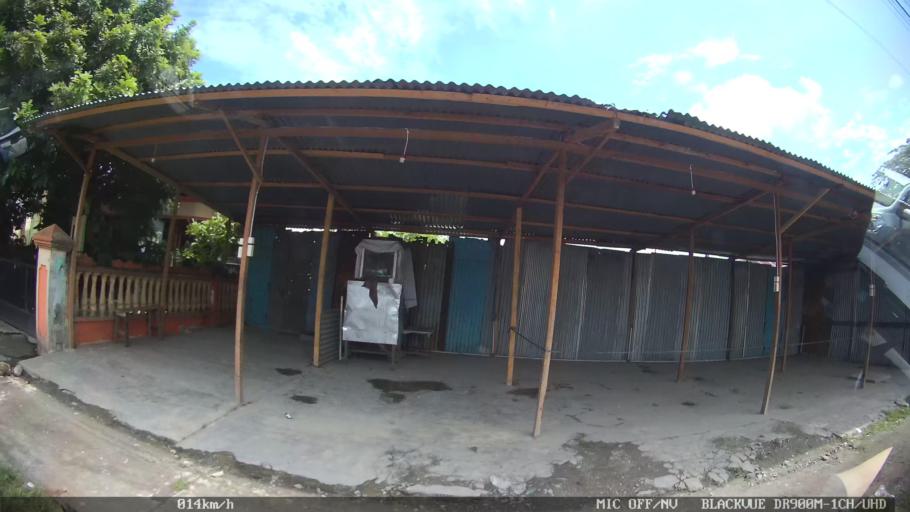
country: ID
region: North Sumatra
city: Medan
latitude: 3.5910
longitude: 98.7518
